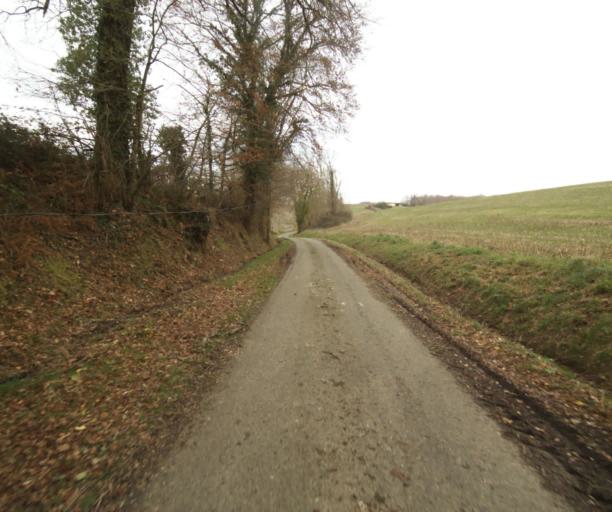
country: FR
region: Midi-Pyrenees
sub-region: Departement du Gers
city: Eauze
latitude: 43.9102
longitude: 0.0523
